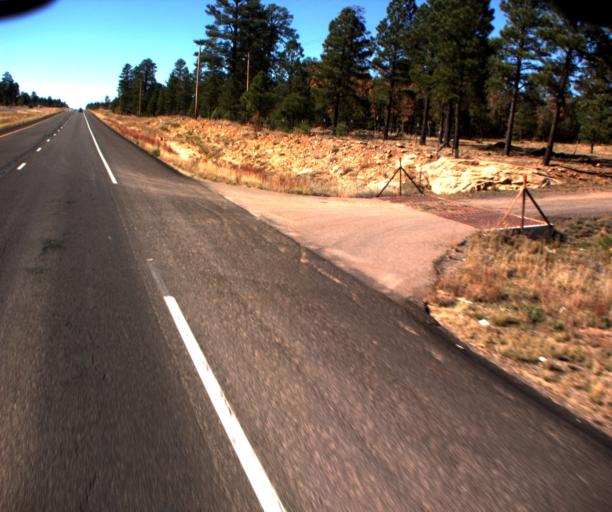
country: US
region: Arizona
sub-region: Apache County
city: Saint Michaels
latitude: 35.6744
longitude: -109.1827
